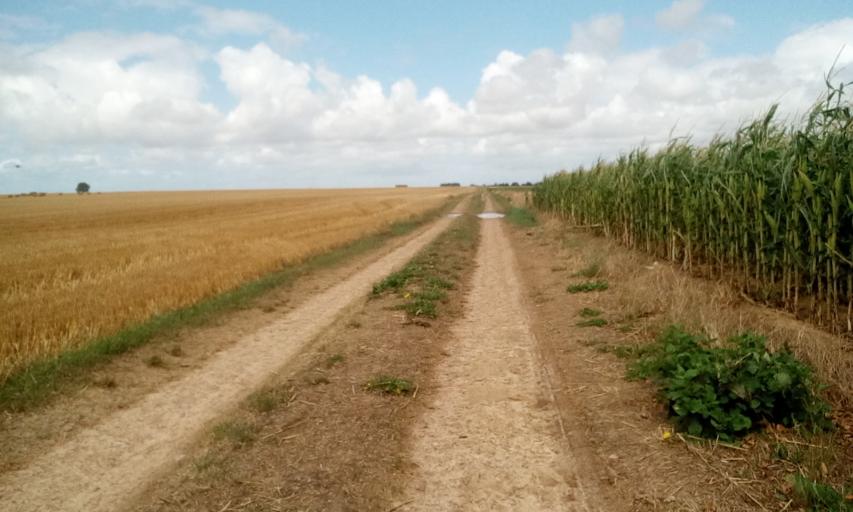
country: FR
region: Lower Normandy
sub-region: Departement du Calvados
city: Cheux
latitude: 49.1724
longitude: -0.5556
